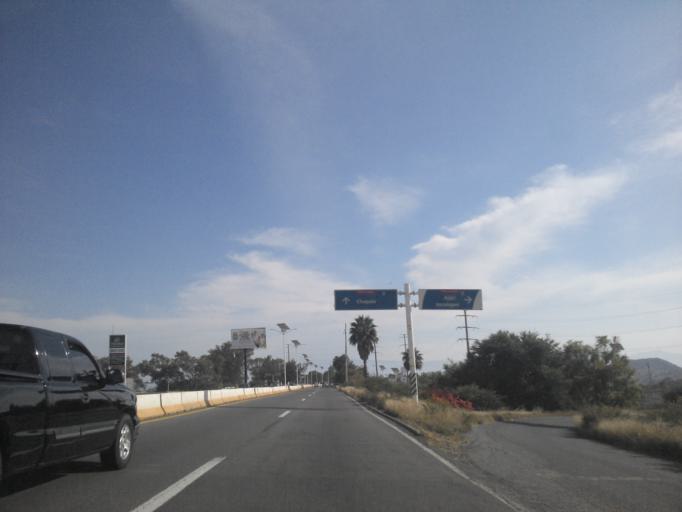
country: MX
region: Jalisco
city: Chapala
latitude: 20.3161
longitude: -103.1955
